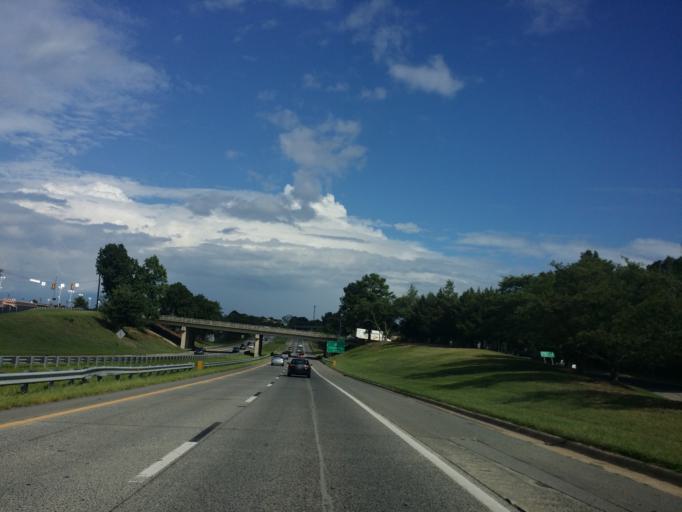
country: US
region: North Carolina
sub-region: Durham County
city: Durham
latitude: 35.9906
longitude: -78.9049
